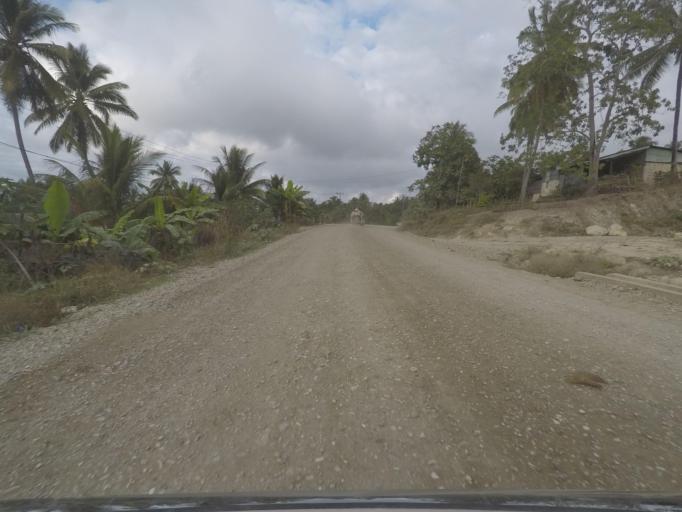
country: TL
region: Baucau
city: Baucau
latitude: -8.5129
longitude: 126.4415
